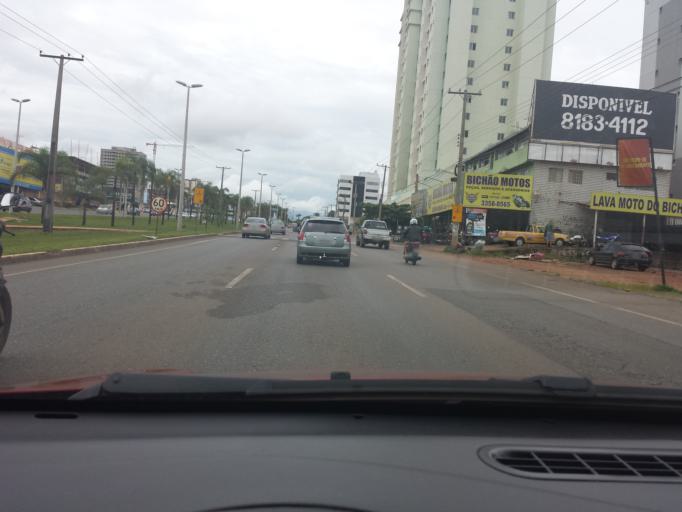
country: BR
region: Federal District
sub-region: Brasilia
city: Brasilia
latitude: -15.8502
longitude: -48.0736
